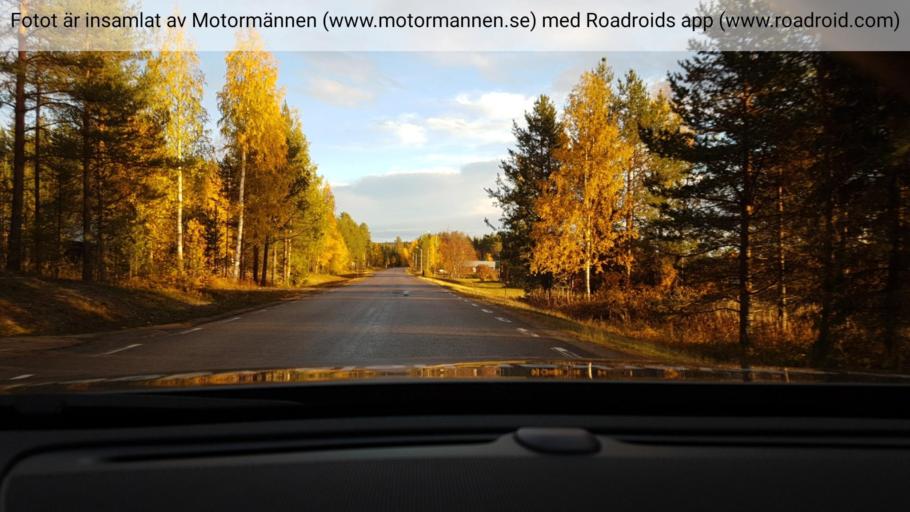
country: SE
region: Norrbotten
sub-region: Overkalix Kommun
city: OEverkalix
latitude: 66.6239
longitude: 22.7407
